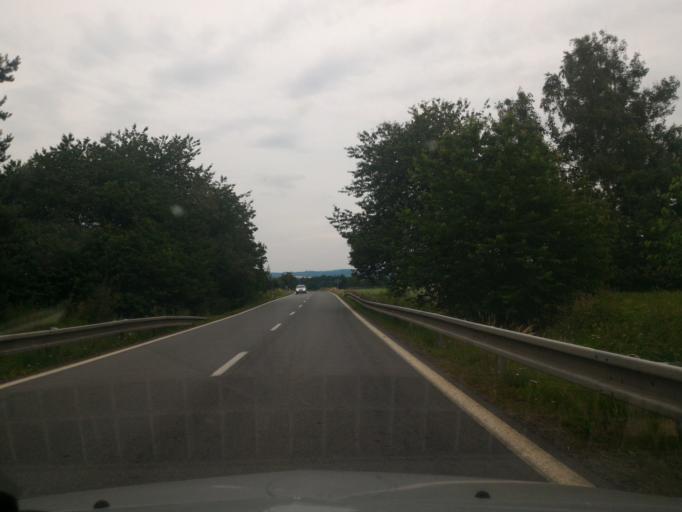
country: CZ
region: Vysocina
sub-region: Okres Jihlava
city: Telc
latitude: 49.1839
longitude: 15.4320
